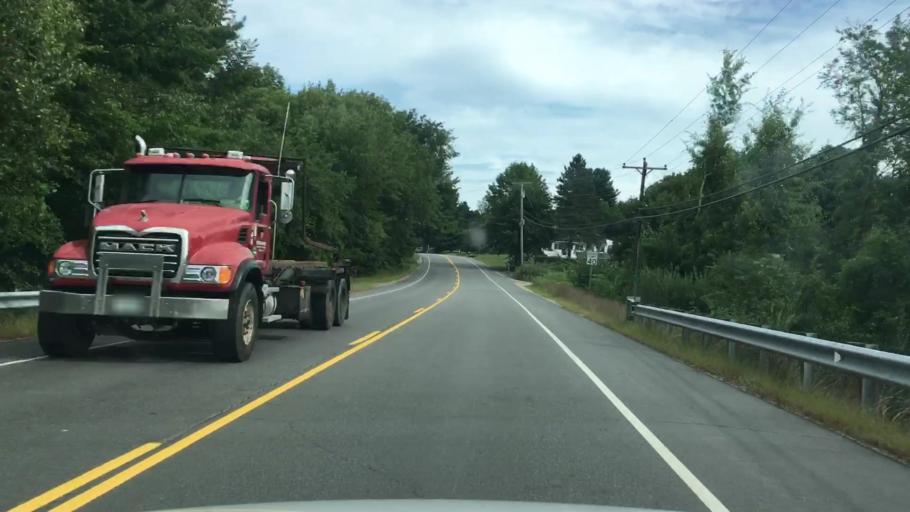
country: US
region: New Hampshire
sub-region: Strafford County
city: Madbury
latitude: 43.1956
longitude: -70.9483
